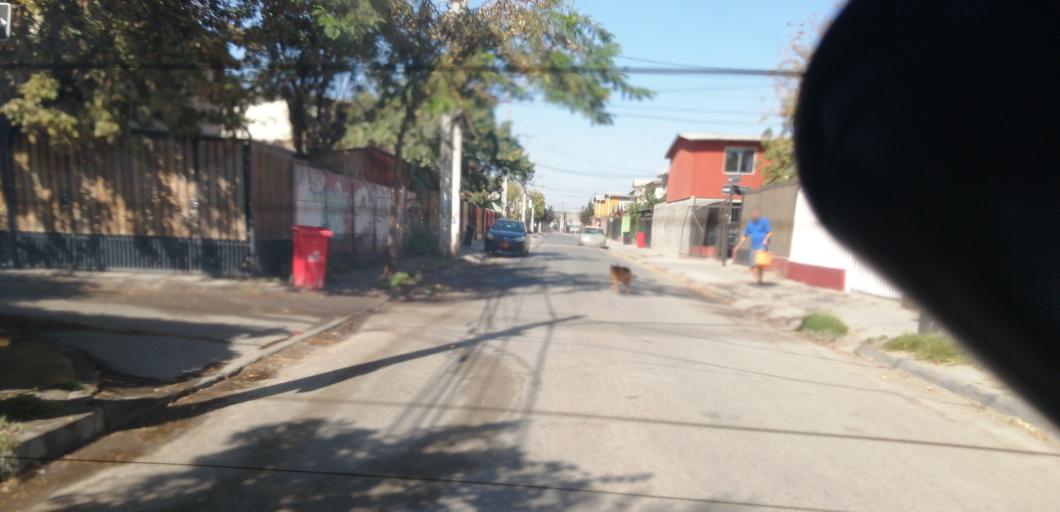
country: CL
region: Santiago Metropolitan
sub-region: Provincia de Santiago
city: Lo Prado
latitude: -33.4623
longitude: -70.7448
